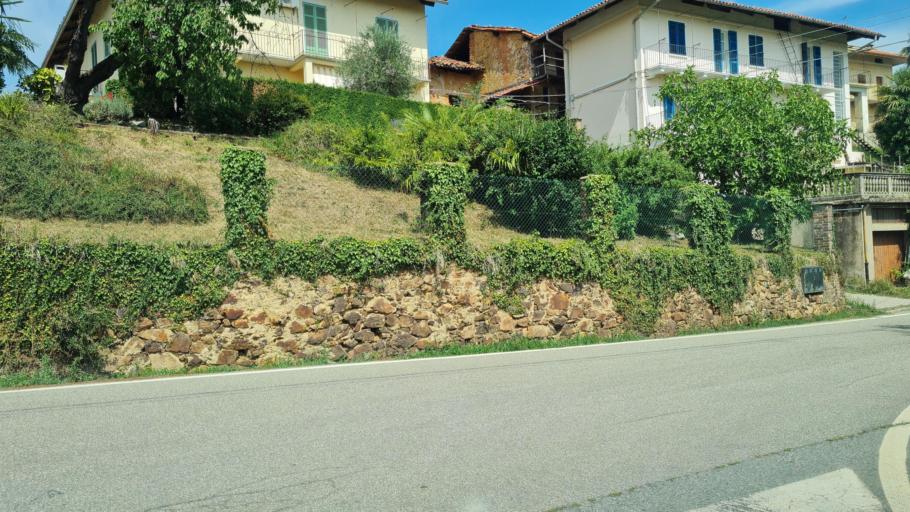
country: IT
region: Piedmont
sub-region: Provincia di Biella
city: Lessona
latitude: 45.5807
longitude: 8.2108
